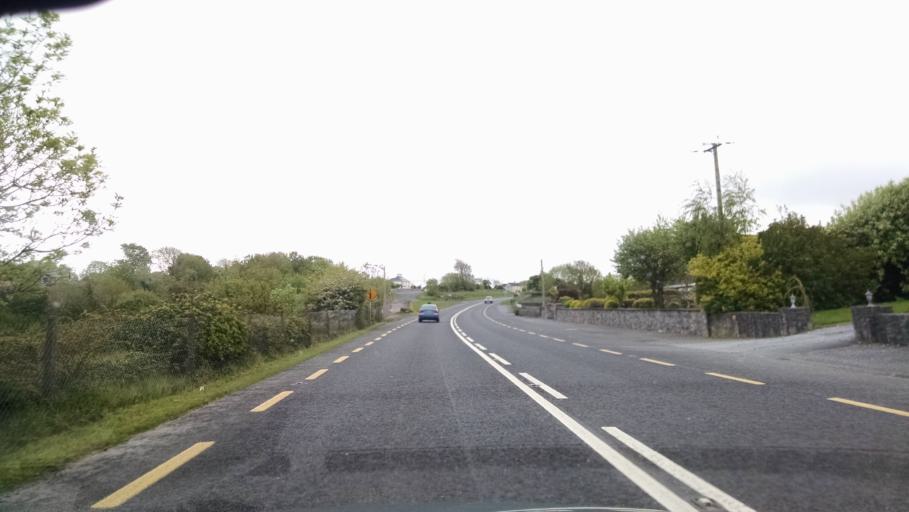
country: IE
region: Connaught
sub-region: County Galway
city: Claregalway
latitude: 53.4117
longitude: -9.0201
